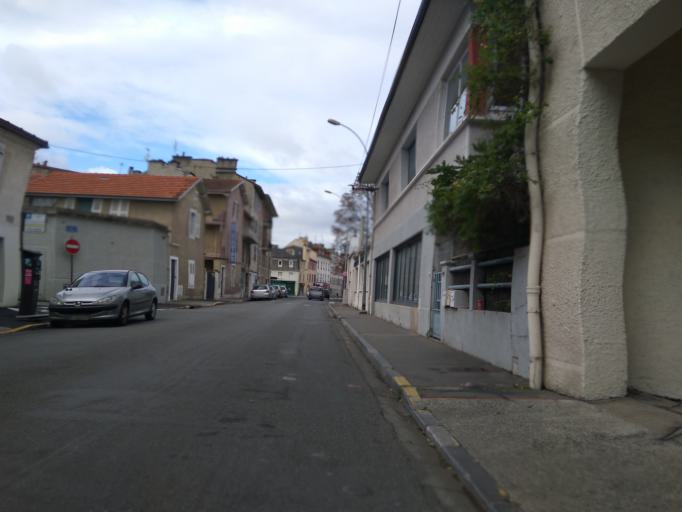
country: FR
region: Aquitaine
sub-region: Departement des Pyrenees-Atlantiques
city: Pau
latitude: 43.3010
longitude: -0.3662
